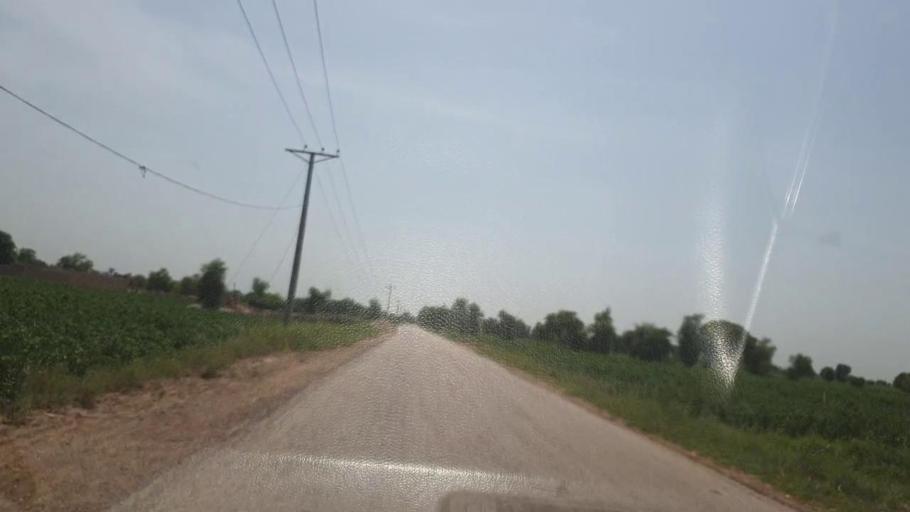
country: PK
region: Sindh
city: Kandiari
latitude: 27.0519
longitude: 68.5495
